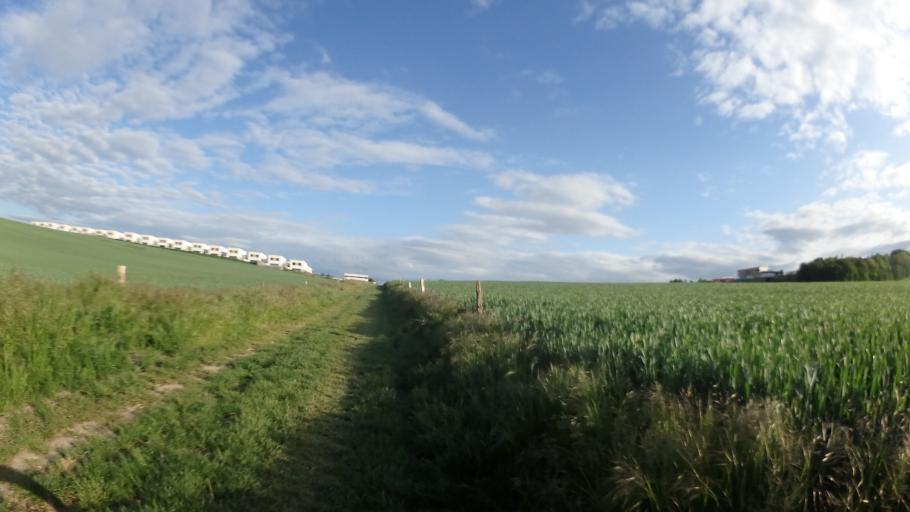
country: CZ
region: South Moravian
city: Moravany
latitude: 49.1537
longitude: 16.5781
